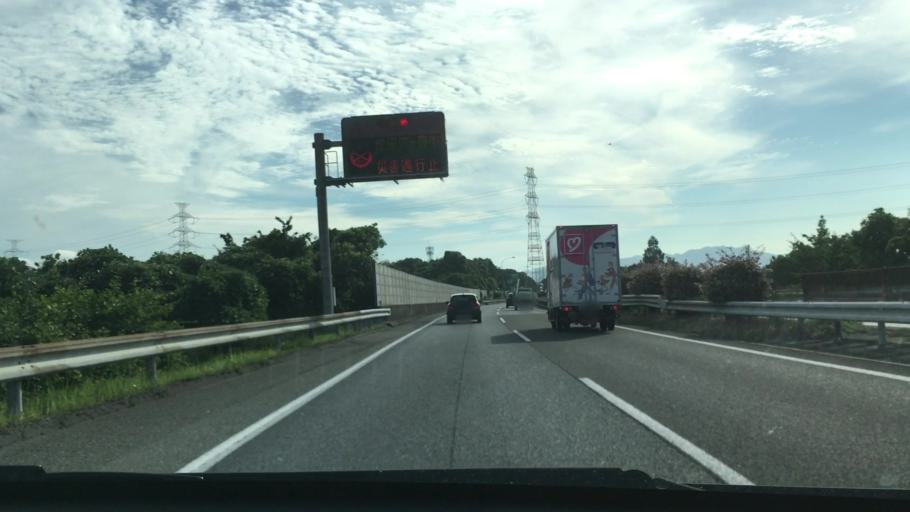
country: JP
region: Fukuoka
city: Kanda
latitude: 33.8340
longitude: 130.9177
